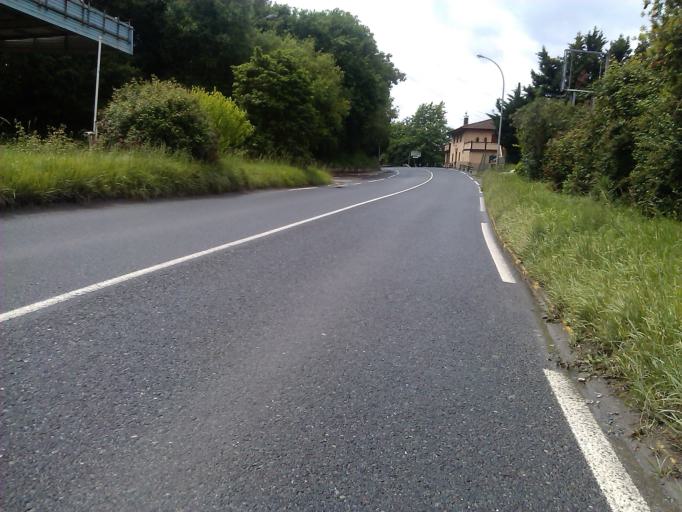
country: ES
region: Basque Country
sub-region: Provincia de Guipuzcoa
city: Urnieta
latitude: 43.2379
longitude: -1.9978
